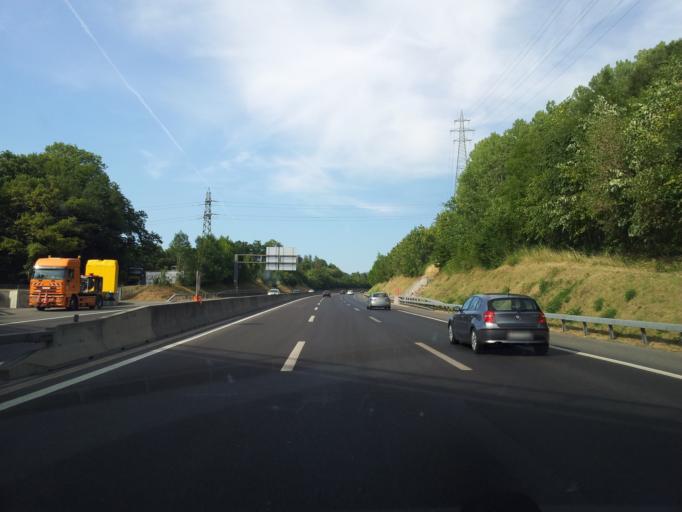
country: CH
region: Vaud
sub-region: Riviera-Pays-d'Enhaut District
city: Jongny
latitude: 46.4782
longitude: 6.8660
